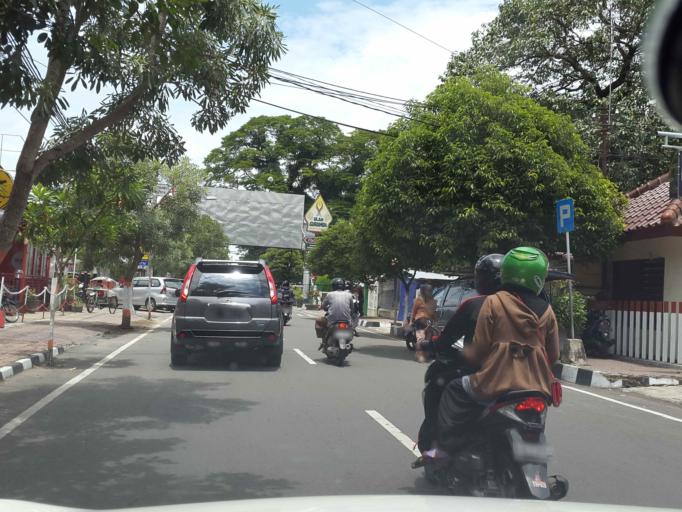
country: ID
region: East Java
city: Mojokerto
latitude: -7.4640
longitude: 112.4352
